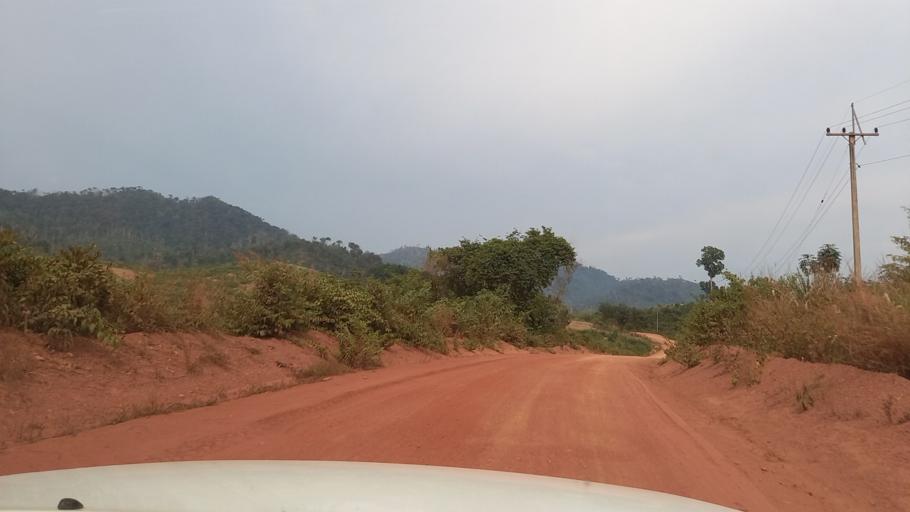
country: LA
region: Bolikhamxai
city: Bolikhan
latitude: 18.5367
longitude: 103.8101
